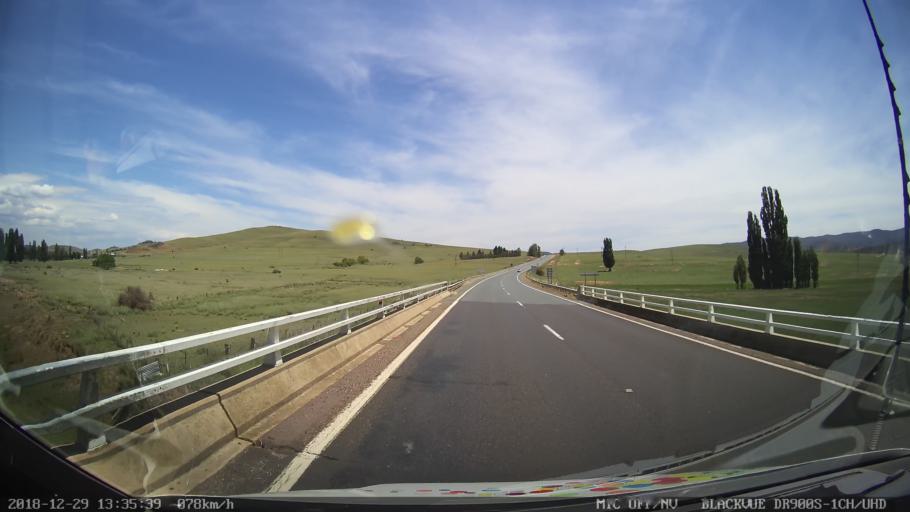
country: AU
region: New South Wales
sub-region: Cooma-Monaro
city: Cooma
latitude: -35.9618
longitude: 149.1483
